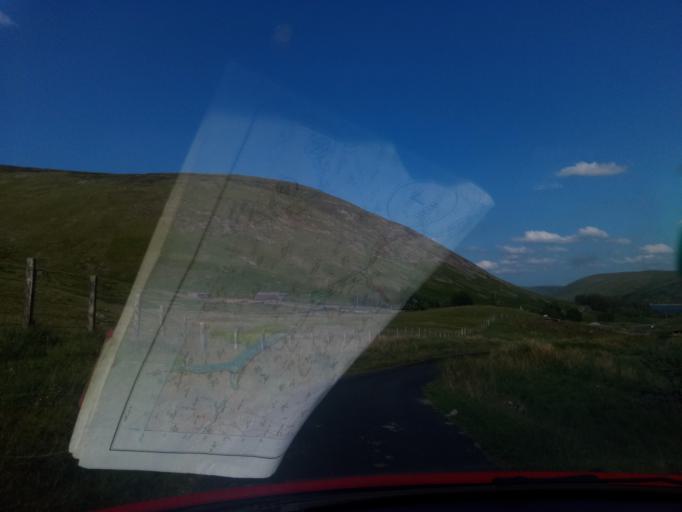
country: GB
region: Scotland
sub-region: Dumfries and Galloway
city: Moffat
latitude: 55.4779
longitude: -3.3191
